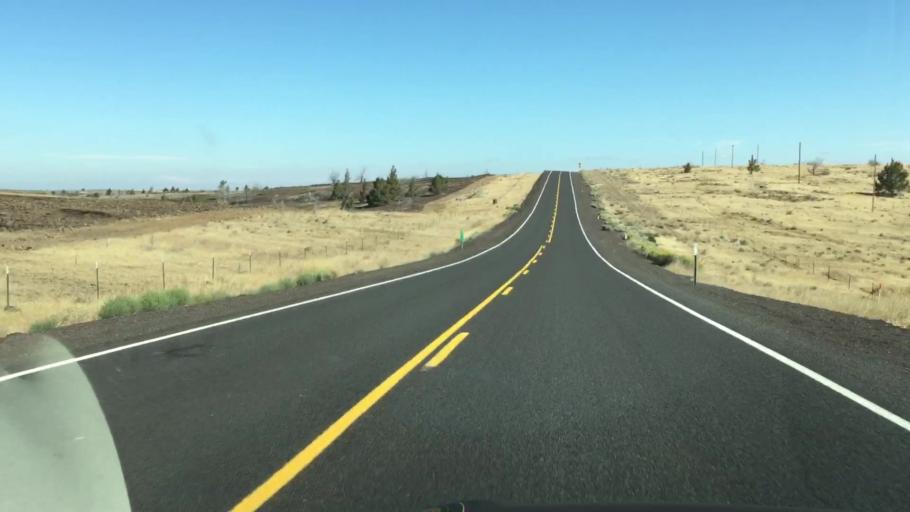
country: US
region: Oregon
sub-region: Jefferson County
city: Warm Springs
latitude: 45.0123
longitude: -120.9905
